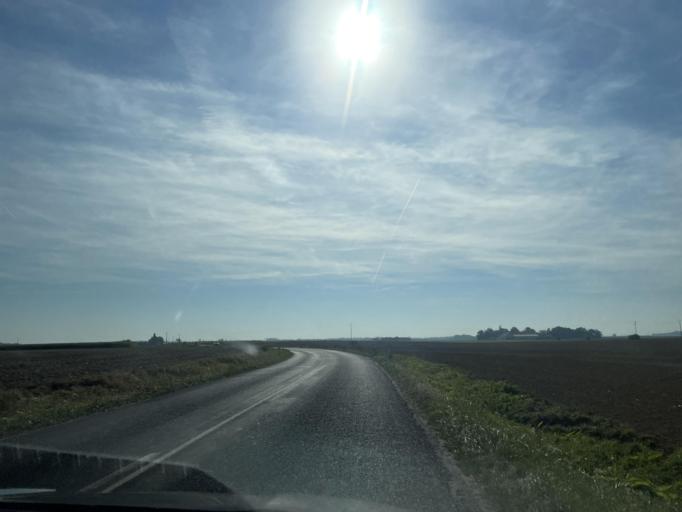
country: FR
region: Ile-de-France
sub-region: Departement de Seine-et-Marne
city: Sammeron
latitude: 48.8842
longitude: 3.0693
